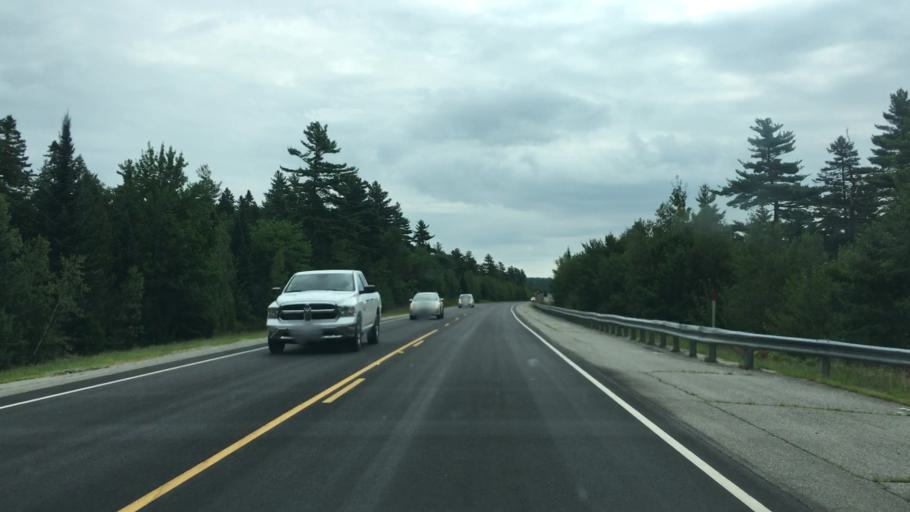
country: US
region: Maine
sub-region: Washington County
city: Addison
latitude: 44.9070
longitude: -67.8297
